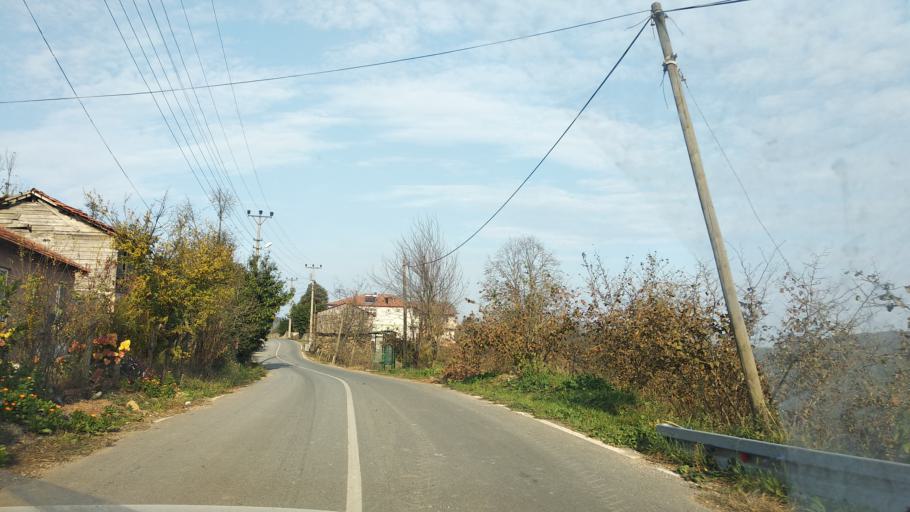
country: TR
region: Sakarya
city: Karasu
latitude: 41.0795
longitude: 30.6075
